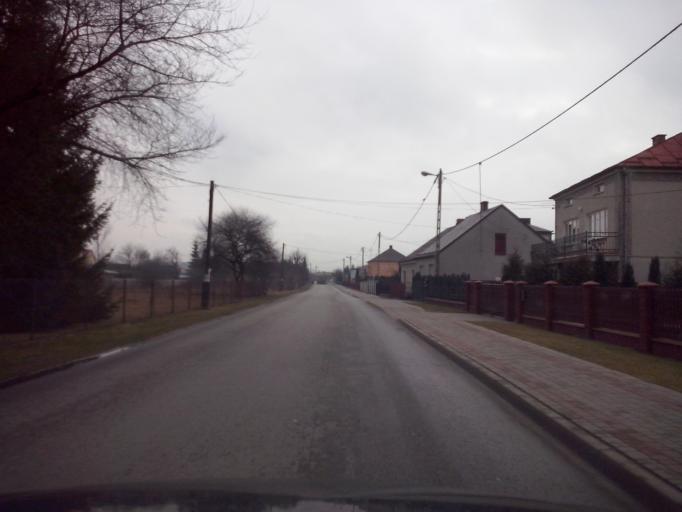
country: PL
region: Subcarpathian Voivodeship
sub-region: Powiat nizanski
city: Ulanow
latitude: 50.4776
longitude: 22.2748
